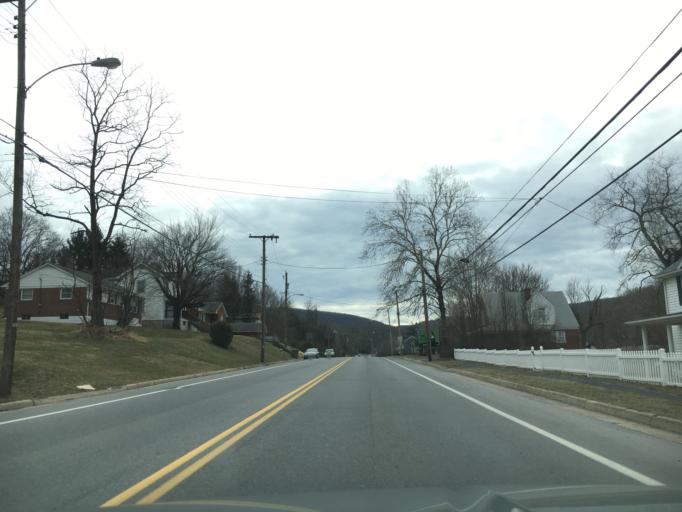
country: US
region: Virginia
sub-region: City of Waynesboro
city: Waynesboro
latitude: 38.0629
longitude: -78.8722
